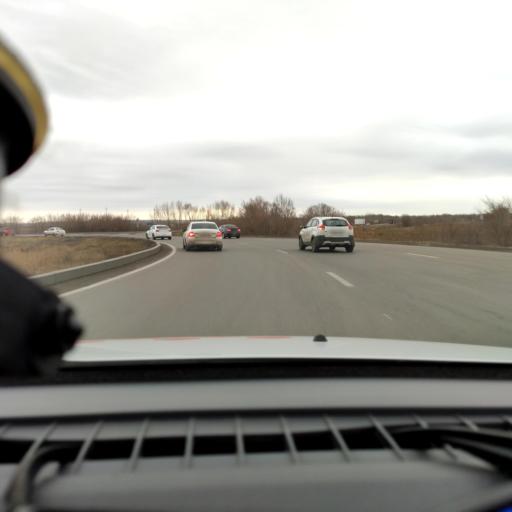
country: RU
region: Samara
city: Samara
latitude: 53.0923
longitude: 50.1501
